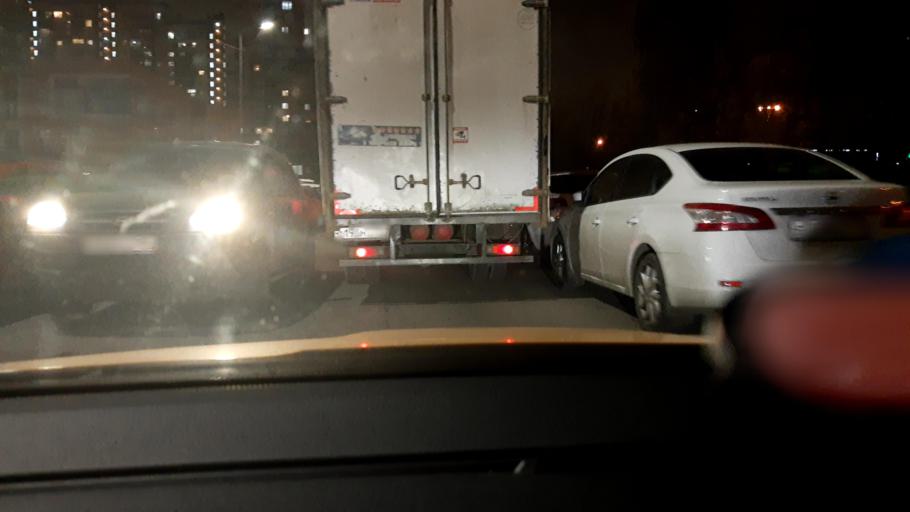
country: RU
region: Moscow
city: Khimki
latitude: 55.8676
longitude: 37.3991
